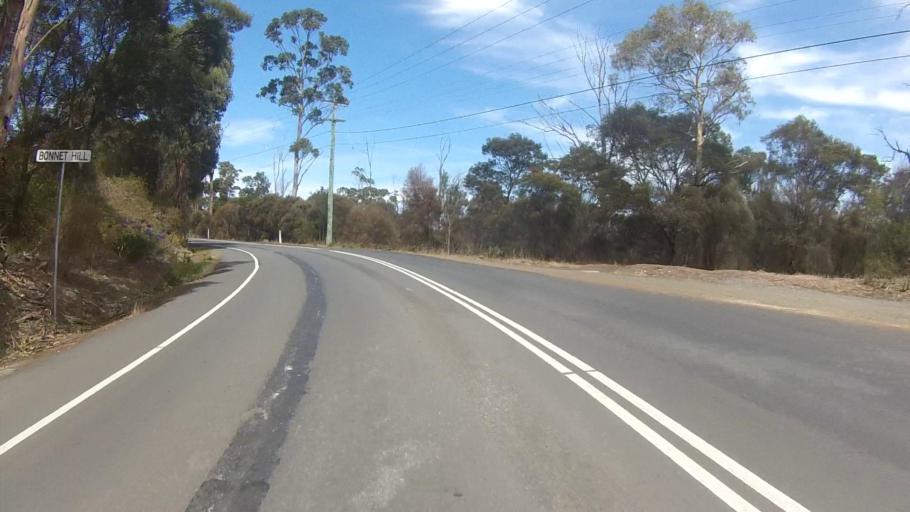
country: AU
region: Tasmania
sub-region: Kingborough
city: Kingston Beach
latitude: -42.9703
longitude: 147.3254
